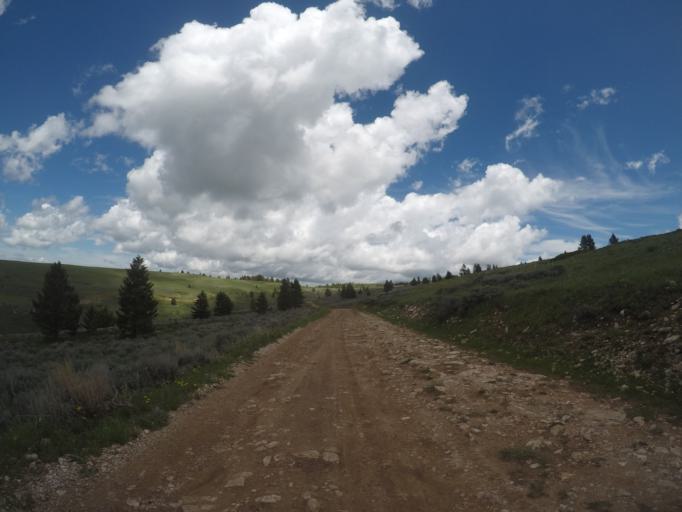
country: US
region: Wyoming
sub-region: Big Horn County
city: Lovell
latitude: 45.1776
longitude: -108.4376
